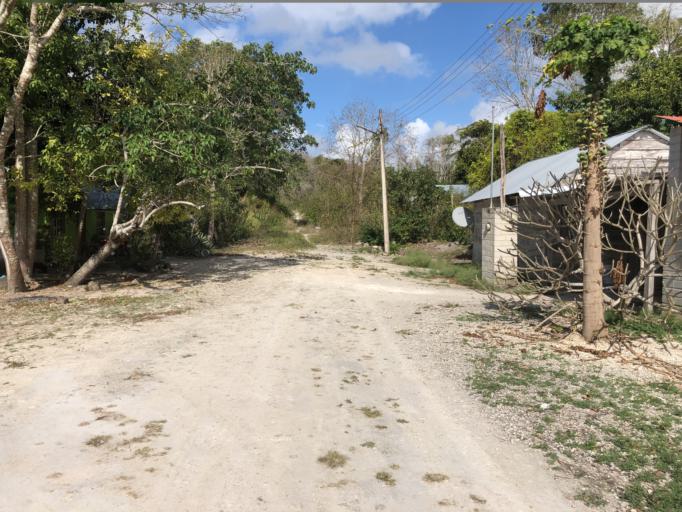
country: MX
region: Quintana Roo
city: Nicolas Bravo
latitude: 18.4553
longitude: -89.3058
